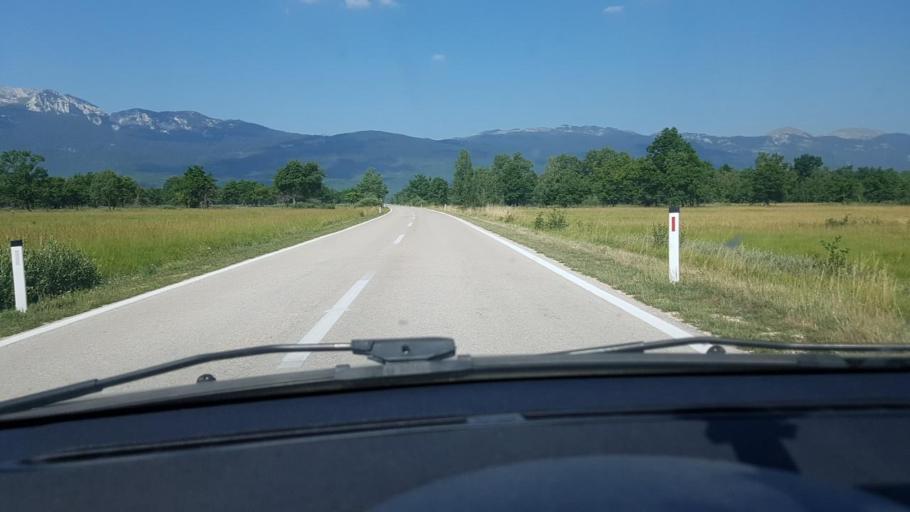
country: BA
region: Federation of Bosnia and Herzegovina
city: Glamoc
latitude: 43.9845
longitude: 16.6854
